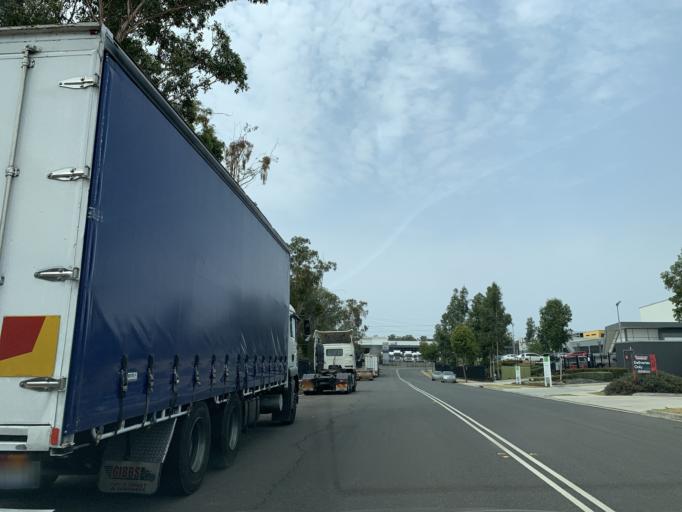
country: AU
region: New South Wales
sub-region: Blacktown
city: Blacktown
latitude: -33.8000
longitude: 150.9000
